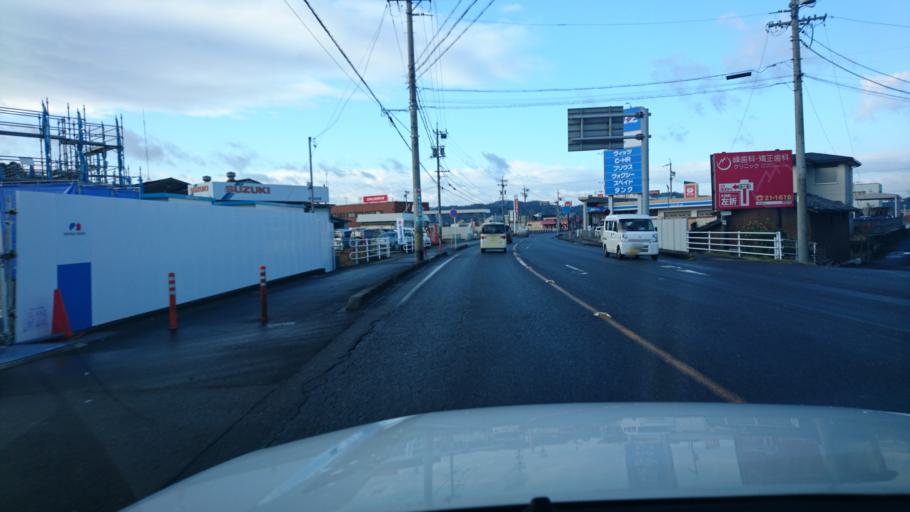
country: JP
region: Mie
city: Ueno-ebisumachi
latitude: 34.7757
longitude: 136.1294
